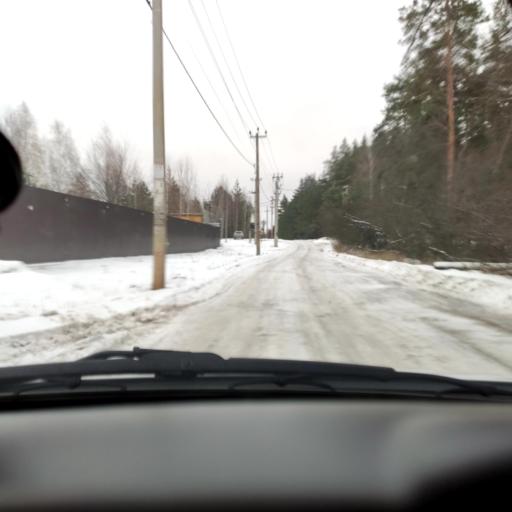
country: RU
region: Voronezj
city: Ramon'
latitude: 51.8863
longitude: 39.2548
